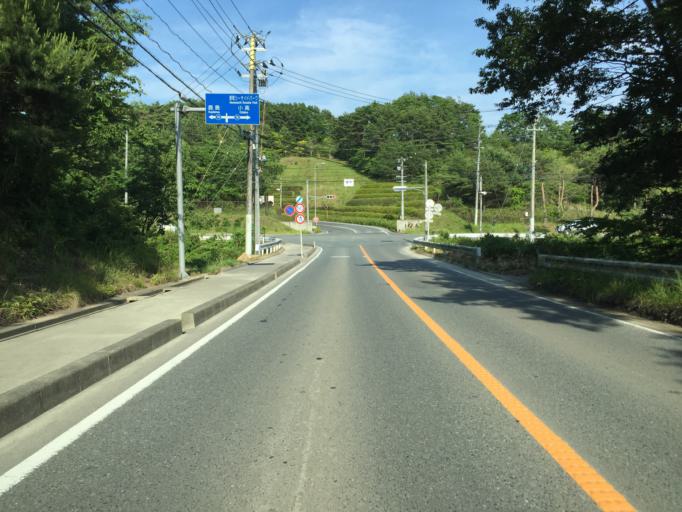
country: JP
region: Fukushima
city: Namie
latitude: 37.6689
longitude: 141.0010
